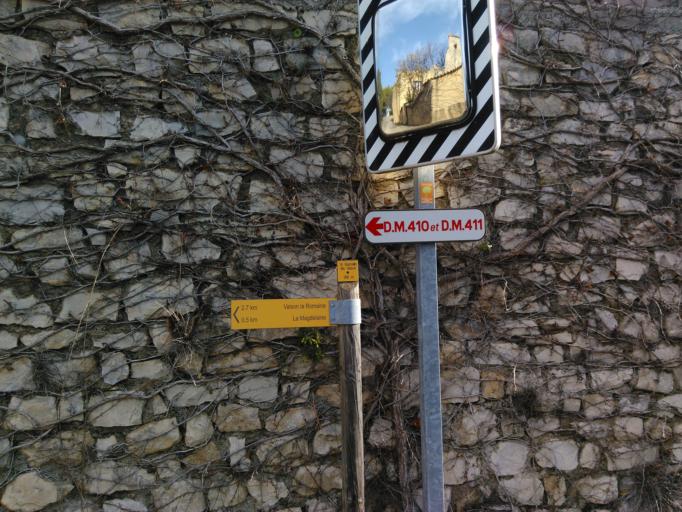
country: FR
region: Provence-Alpes-Cote d'Azur
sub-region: Departement du Vaucluse
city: Vaison-la-Romaine
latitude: 44.2305
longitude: 5.0990
